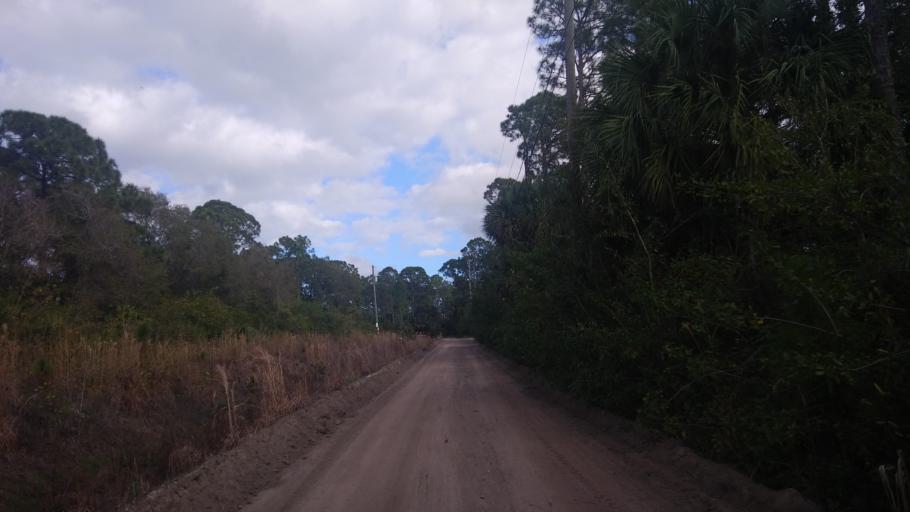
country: US
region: Florida
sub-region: Indian River County
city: Fellsmere
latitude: 27.7571
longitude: -80.5780
